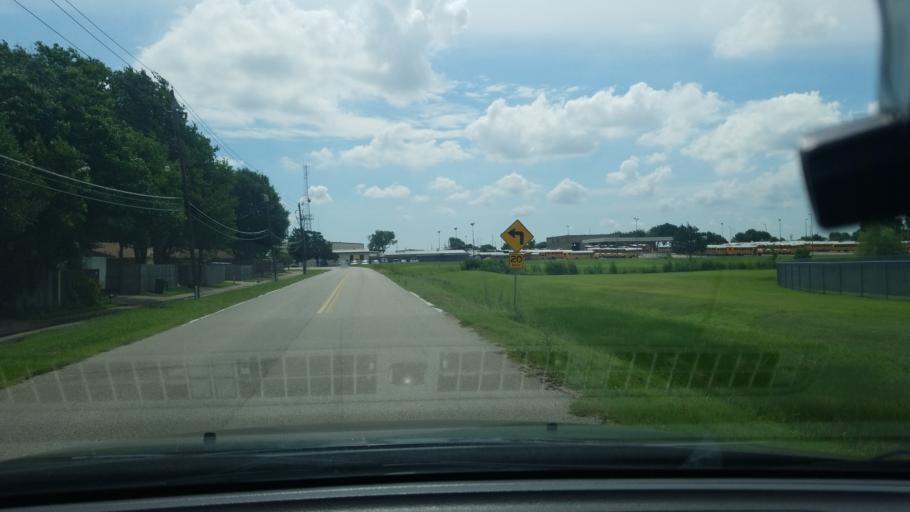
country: US
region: Texas
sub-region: Dallas County
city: Mesquite
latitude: 32.7686
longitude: -96.5924
